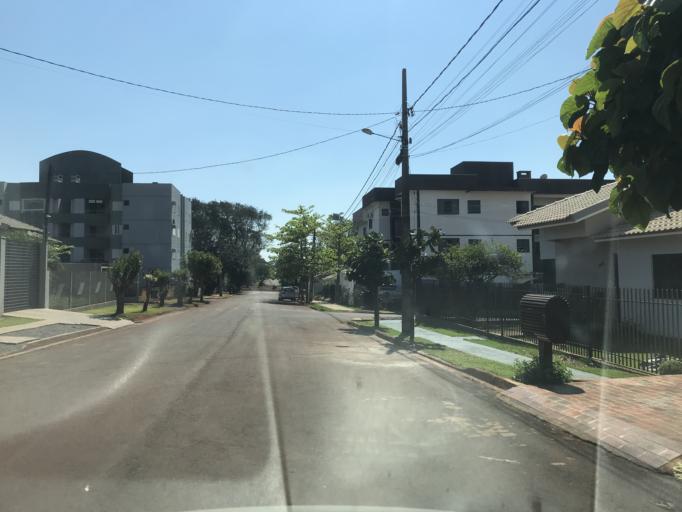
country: BR
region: Parana
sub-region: Palotina
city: Palotina
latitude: -24.2922
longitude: -53.8346
